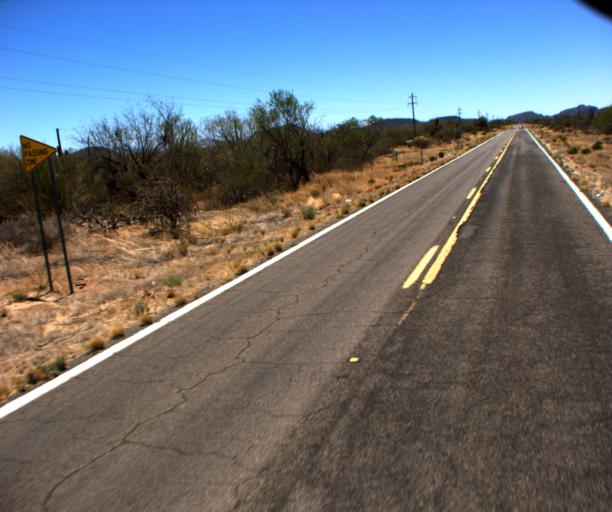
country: US
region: Arizona
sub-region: Pima County
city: Sells
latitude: 32.0180
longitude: -111.9997
